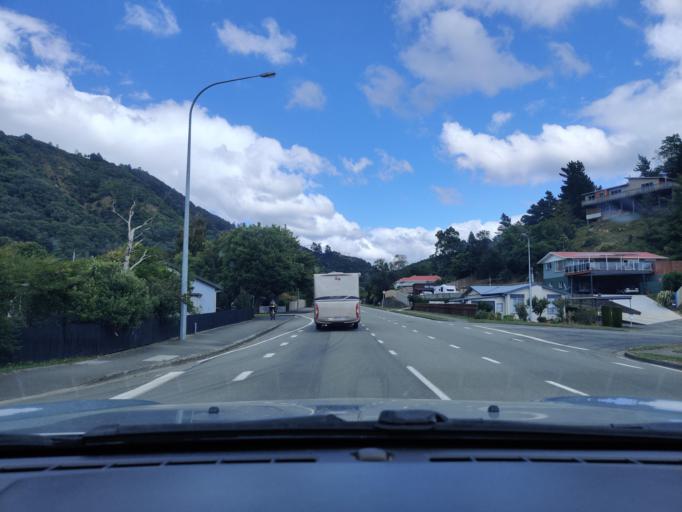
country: NZ
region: Marlborough
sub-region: Marlborough District
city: Picton
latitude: -41.2981
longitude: 174.0000
